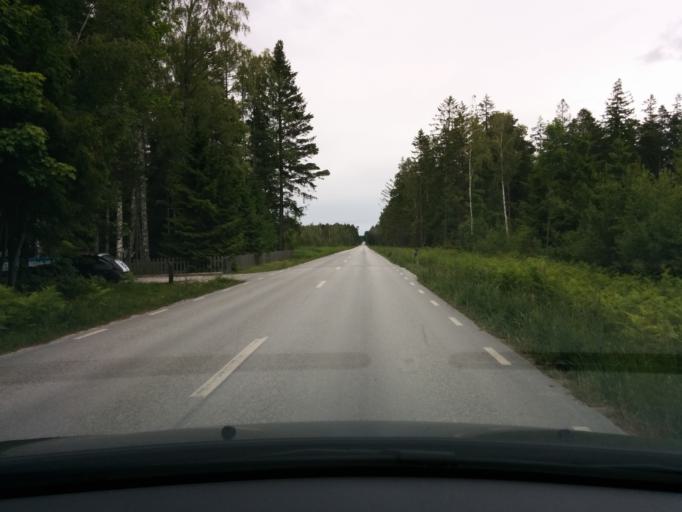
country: SE
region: Gotland
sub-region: Gotland
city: Slite
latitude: 57.6341
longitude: 18.7630
